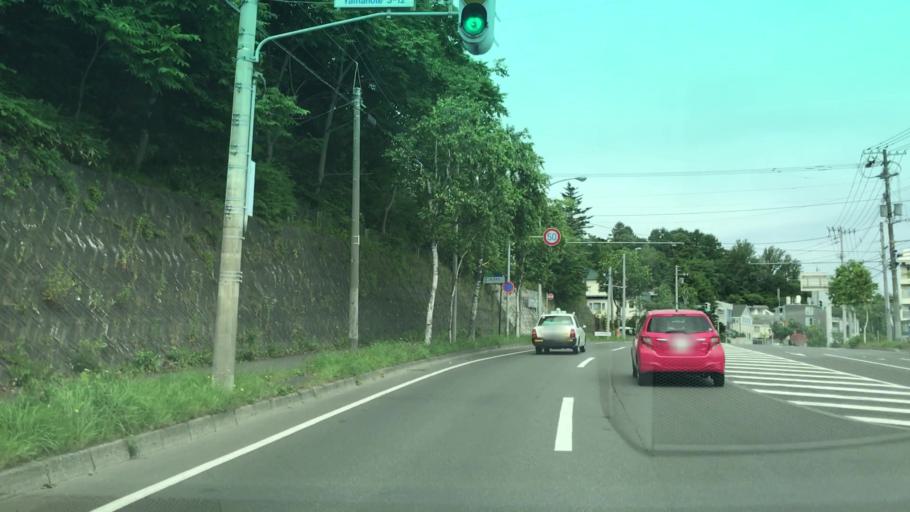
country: JP
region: Hokkaido
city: Sapporo
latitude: 43.0646
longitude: 141.2899
